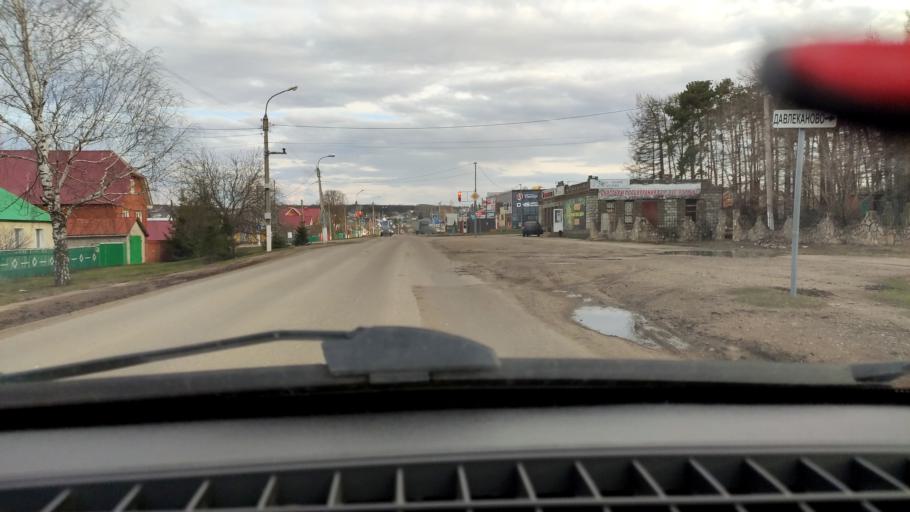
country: RU
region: Bashkortostan
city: Tolbazy
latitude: 54.0265
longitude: 55.8850
